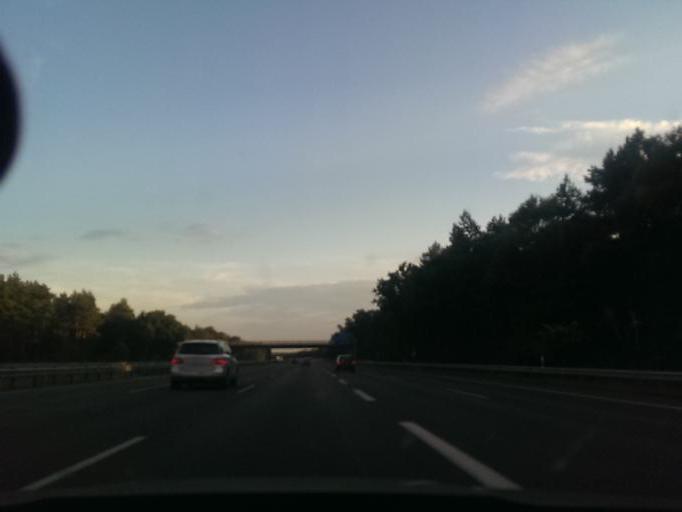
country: DE
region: Lower Saxony
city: Hademstorf
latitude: 52.7775
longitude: 9.6686
